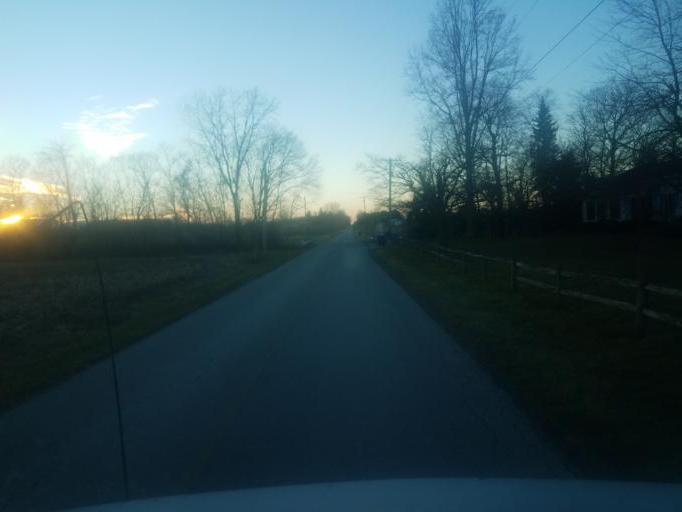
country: US
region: Ohio
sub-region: Richland County
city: Ontario
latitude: 40.8430
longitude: -82.5815
